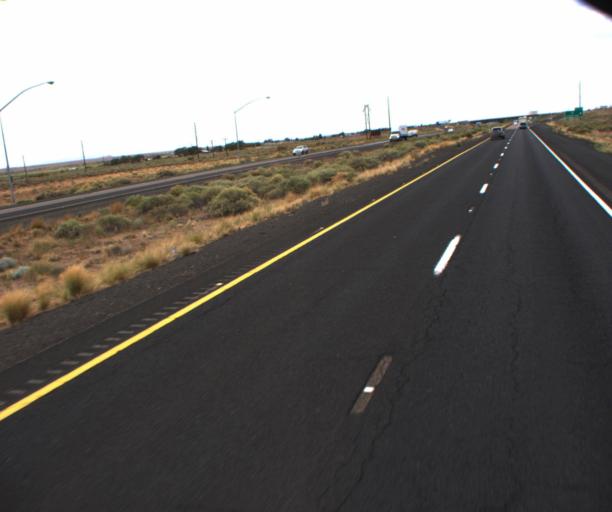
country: US
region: Arizona
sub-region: Navajo County
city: Joseph City
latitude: 34.9498
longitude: -110.3036
